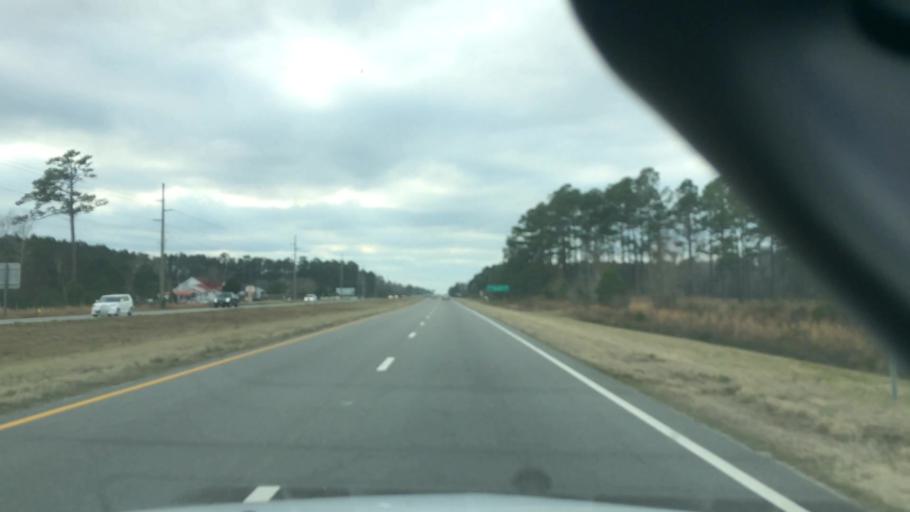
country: US
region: North Carolina
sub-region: Brunswick County
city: Sunset Beach
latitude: 33.9462
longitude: -78.5050
